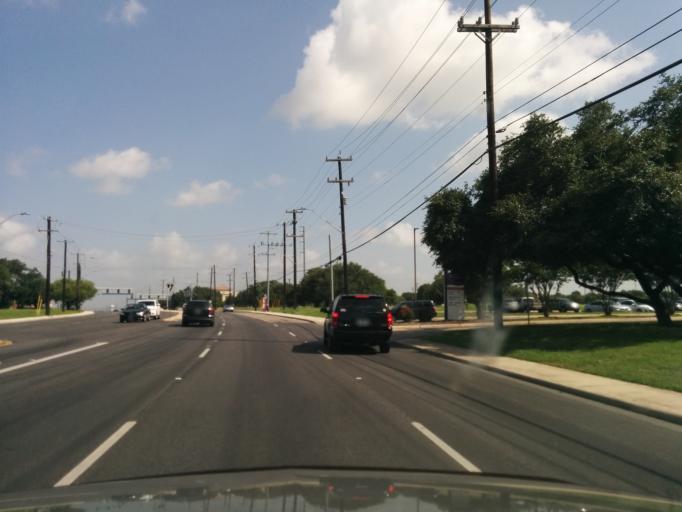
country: US
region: Texas
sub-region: Bexar County
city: Leon Valley
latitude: 29.5141
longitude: -98.5919
